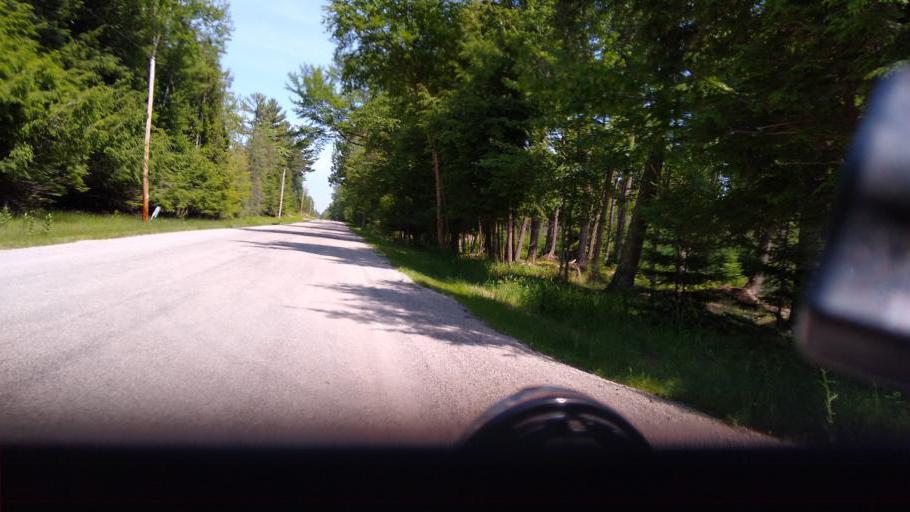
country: US
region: Michigan
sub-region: Delta County
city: Escanaba
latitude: 45.7101
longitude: -87.1565
